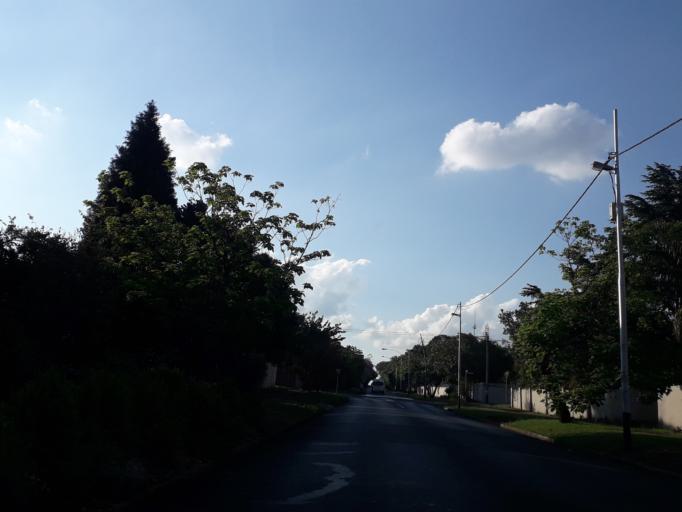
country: ZA
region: Gauteng
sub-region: City of Johannesburg Metropolitan Municipality
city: Johannesburg
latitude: -26.1413
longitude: 27.9991
